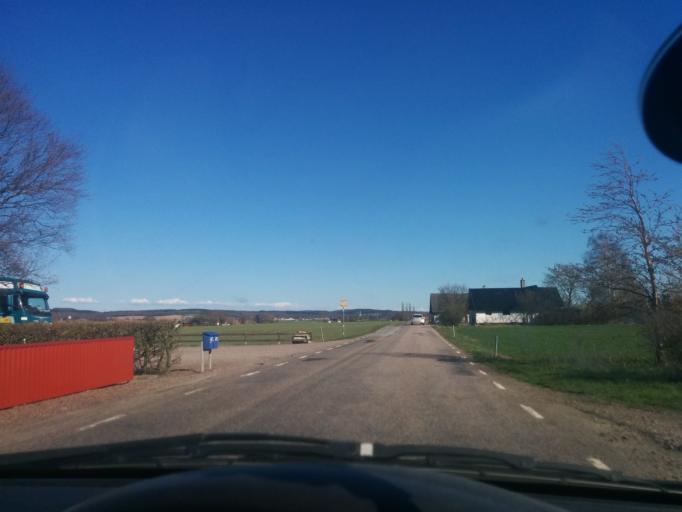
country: SE
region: Skane
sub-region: Lunds Kommun
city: Genarp
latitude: 55.6114
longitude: 13.3556
